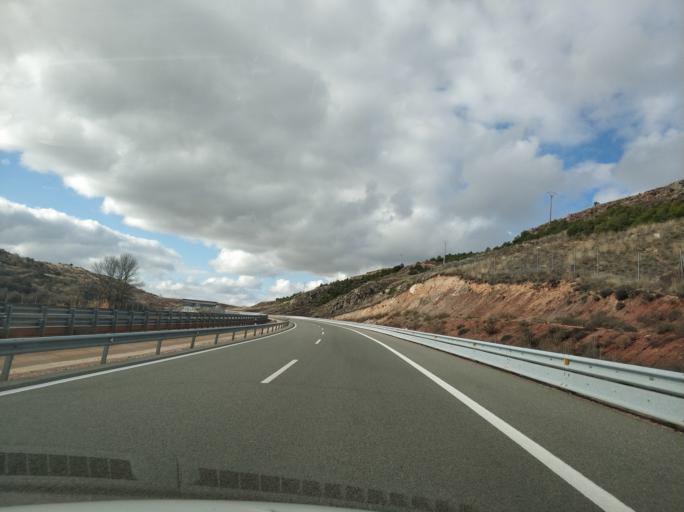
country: ES
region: Castille and Leon
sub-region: Provincia de Soria
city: Medinaceli
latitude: 41.1934
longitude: -2.4368
